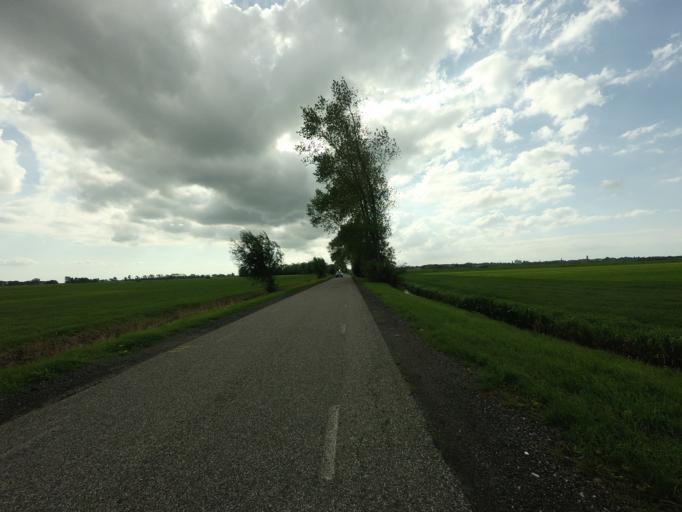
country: NL
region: Friesland
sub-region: Sudwest Fryslan
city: Bolsward
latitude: 53.0646
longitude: 5.5644
